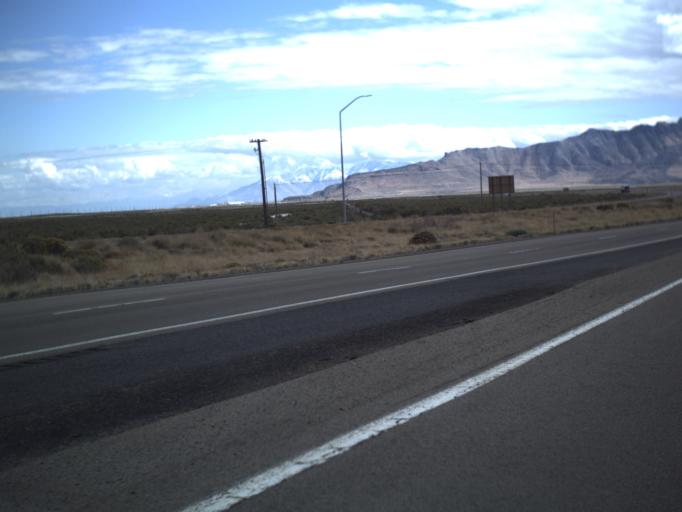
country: US
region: Utah
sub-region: Tooele County
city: Grantsville
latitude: 40.7608
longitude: -112.7784
